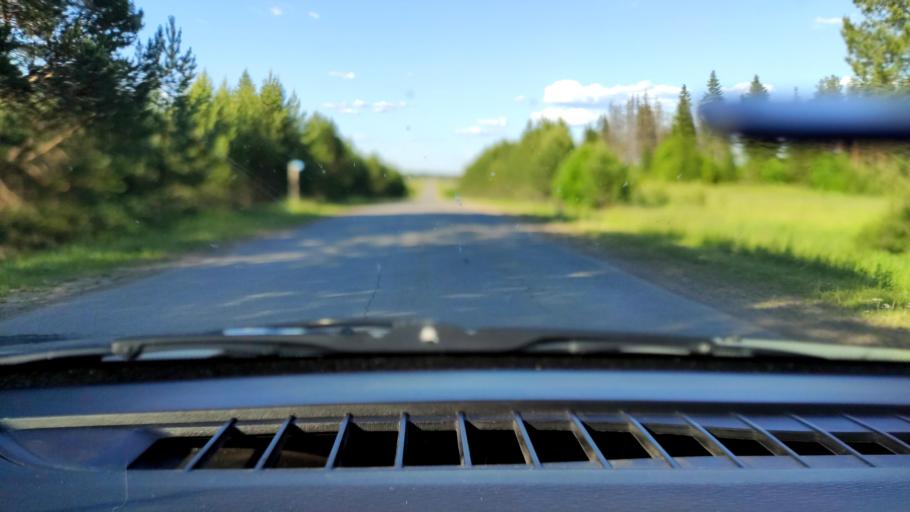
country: RU
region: Perm
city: Uinskoye
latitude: 57.0861
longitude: 56.6236
